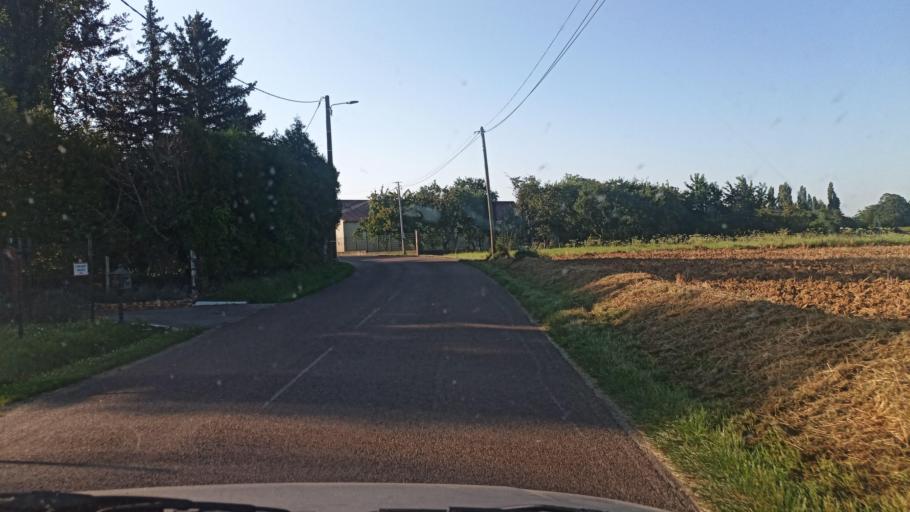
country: FR
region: Bourgogne
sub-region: Departement de l'Yonne
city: Saint-Valerien
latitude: 48.1958
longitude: 3.1186
